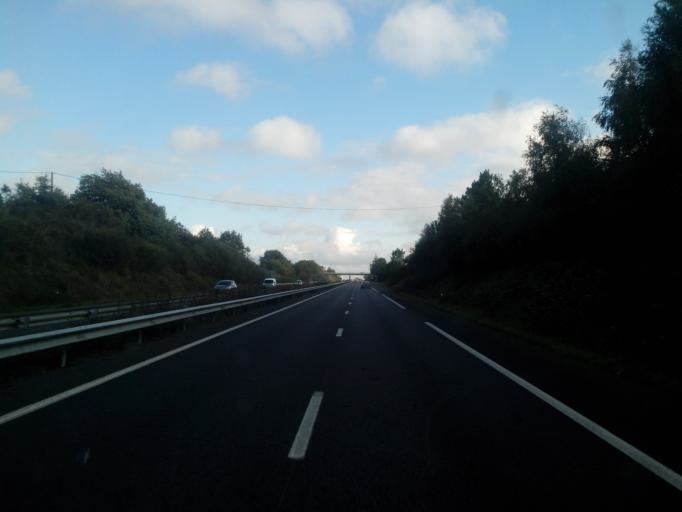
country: FR
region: Brittany
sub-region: Departement du Morbihan
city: Nivillac
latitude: 47.5112
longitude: -2.2746
